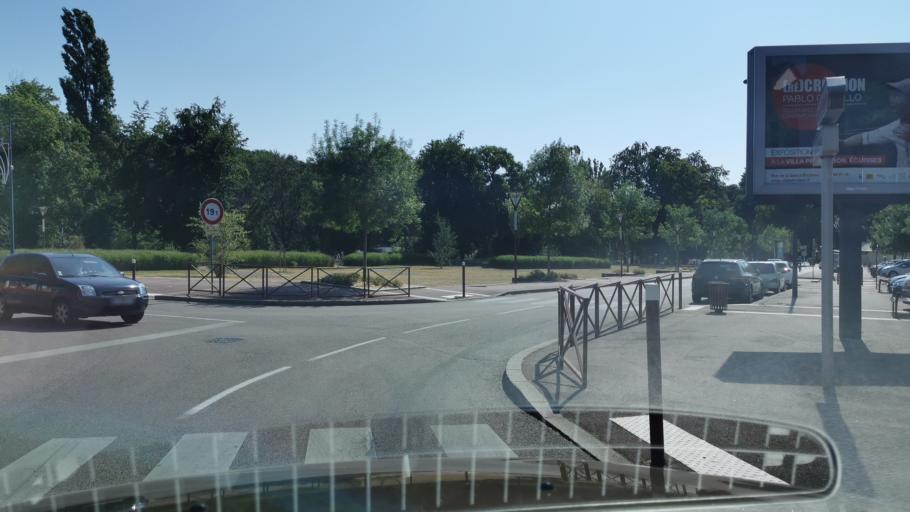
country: FR
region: Bourgogne
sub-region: Departement de Saone-et-Loire
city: Le Creusot
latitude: 46.8021
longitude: 4.4182
